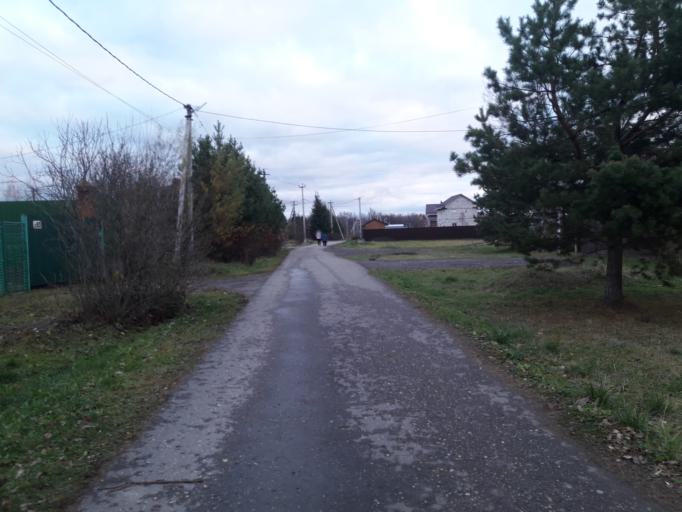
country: RU
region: Moskovskaya
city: Ashukino
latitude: 56.1733
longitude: 37.9360
